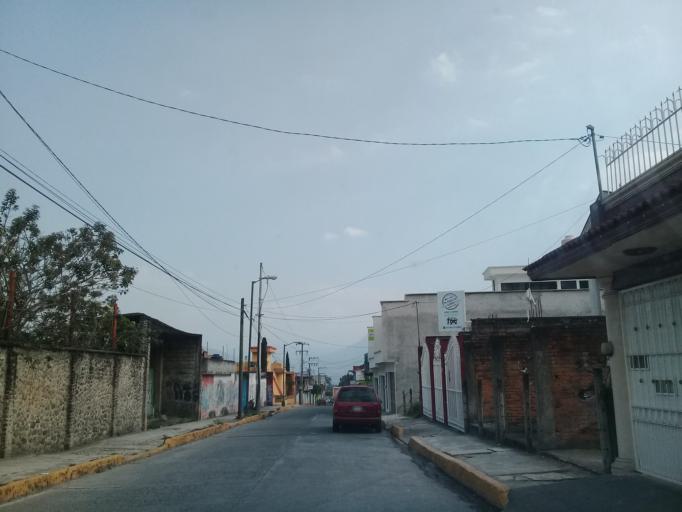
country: MX
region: Veracruz
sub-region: Ixhuatlancillo
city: Union y Progreso
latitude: 18.8684
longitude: -97.1068
